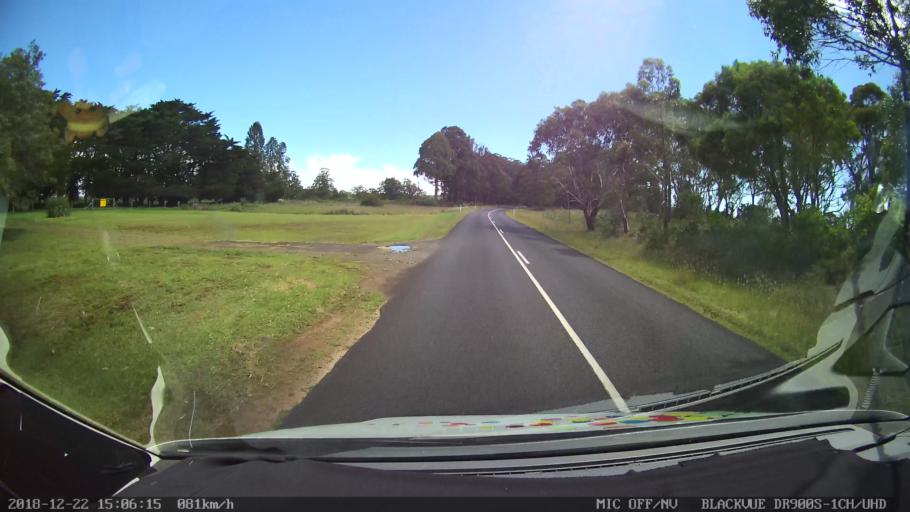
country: AU
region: New South Wales
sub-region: Bellingen
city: Dorrigo
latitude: -30.2919
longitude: 152.4291
